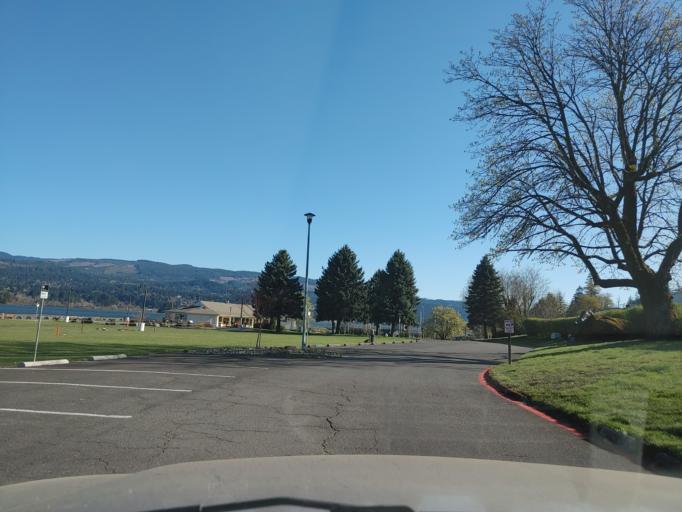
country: US
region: Oregon
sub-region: Hood River County
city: Cascade Locks
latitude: 45.6700
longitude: -121.8933
